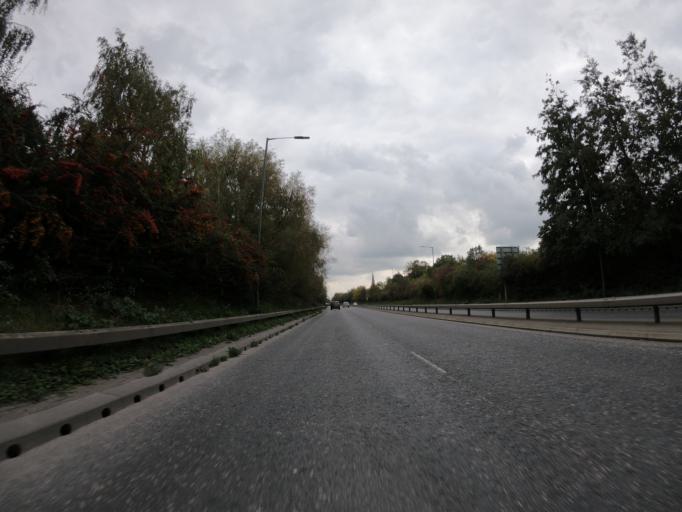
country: GB
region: England
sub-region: Greater London
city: Erith
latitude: 51.4839
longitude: 0.1728
